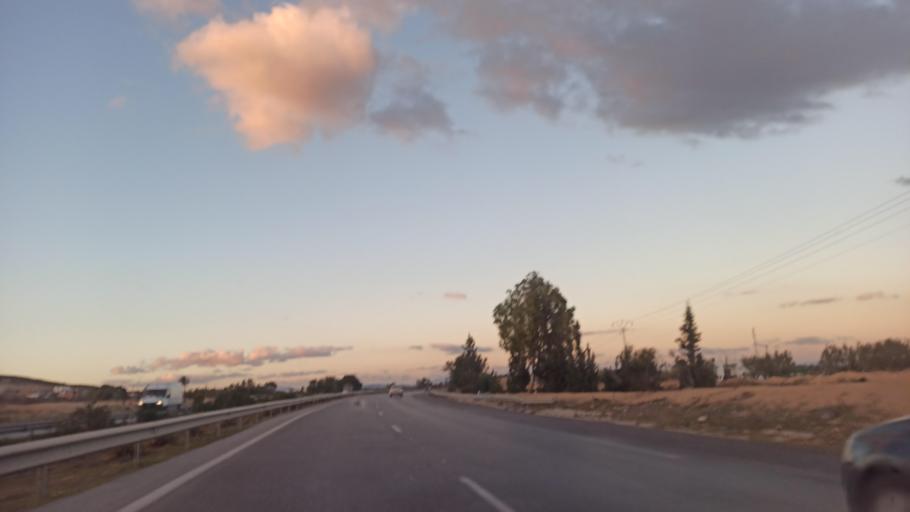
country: TN
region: Susah
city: Harqalah
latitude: 36.2311
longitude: 10.4131
